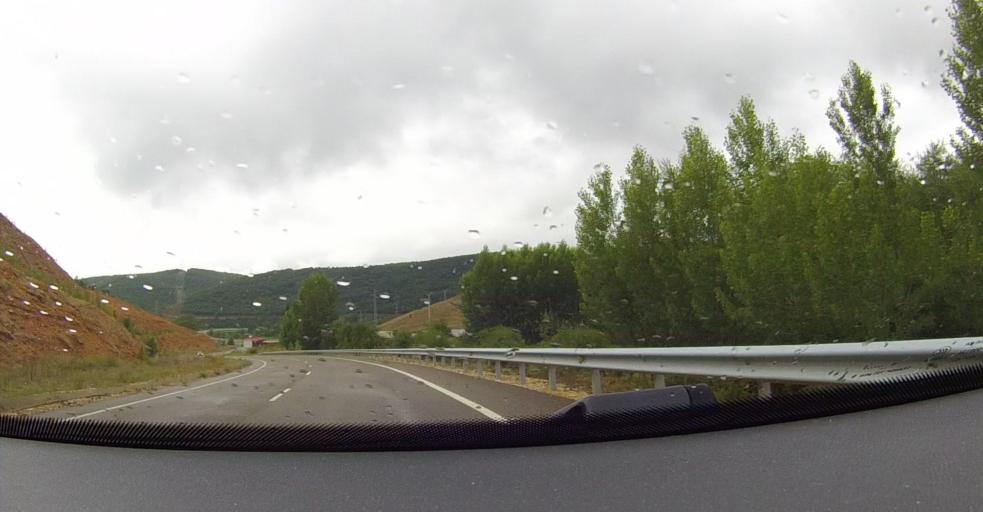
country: ES
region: Castille and Leon
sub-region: Provincia de Leon
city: Cistierna
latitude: 42.7954
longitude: -5.1213
